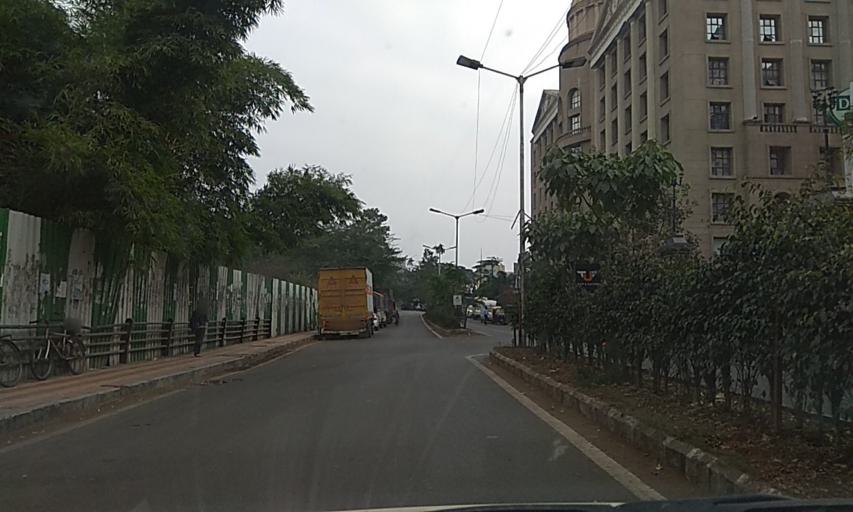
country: IN
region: Maharashtra
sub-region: Pune Division
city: Lohogaon
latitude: 18.5454
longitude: 73.9100
